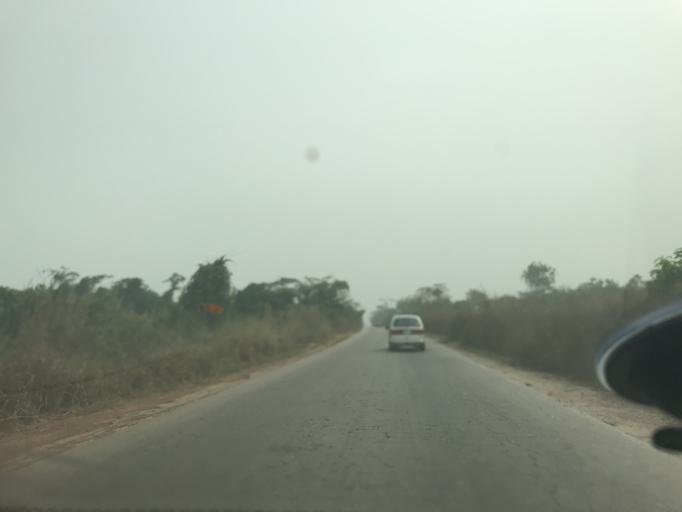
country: NG
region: Ogun
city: Ilaro
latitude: 6.8836
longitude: 3.0897
